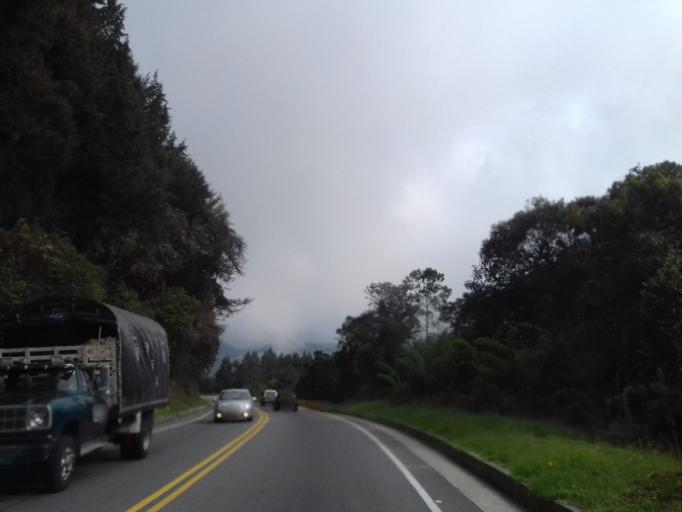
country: CO
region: Caldas
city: Villamaria
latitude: 5.0169
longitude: -75.3631
